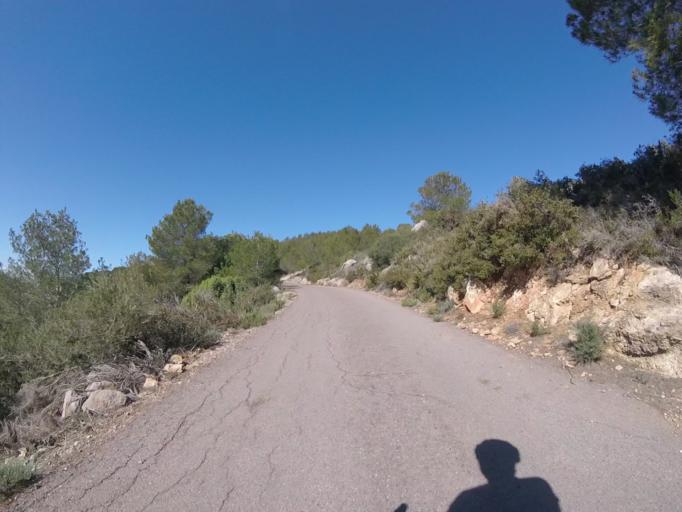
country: ES
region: Valencia
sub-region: Provincia de Castello
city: Benicassim
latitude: 40.0788
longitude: 0.0913
